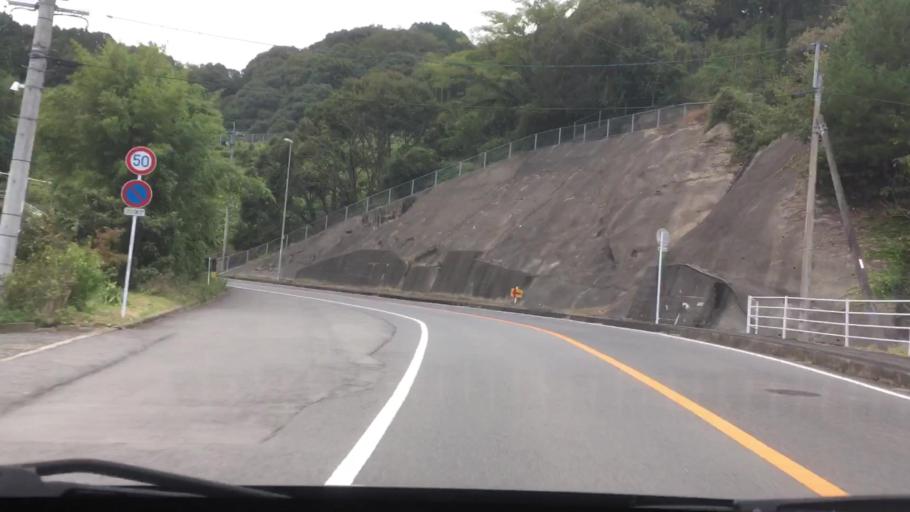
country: JP
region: Nagasaki
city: Sasebo
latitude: 33.0018
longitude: 129.7282
